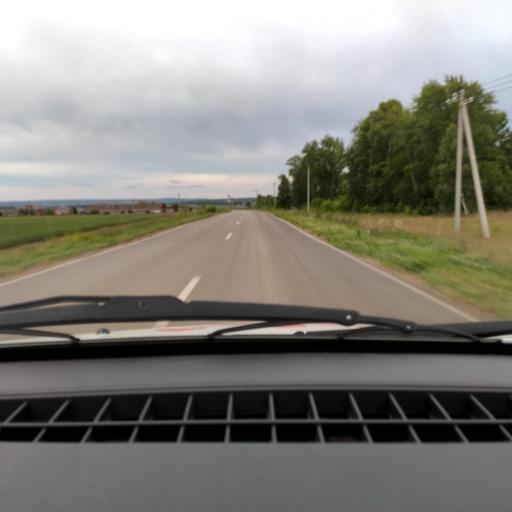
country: RU
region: Bashkortostan
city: Avdon
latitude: 54.5171
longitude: 55.7722
